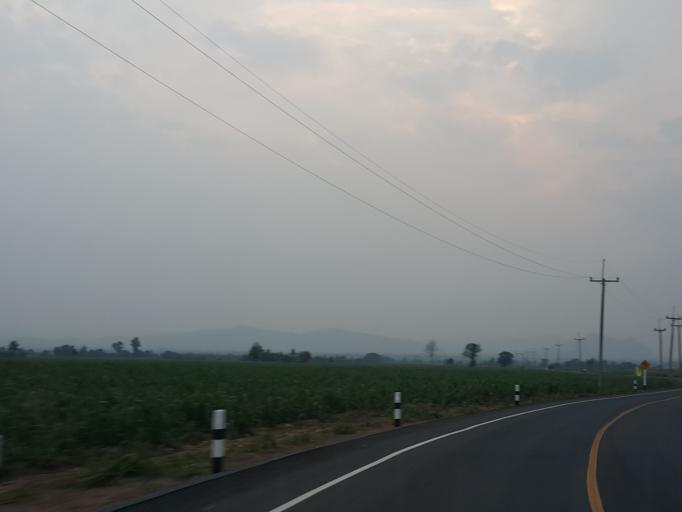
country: TH
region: Suphan Buri
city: Dan Chang
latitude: 14.9436
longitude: 99.6561
